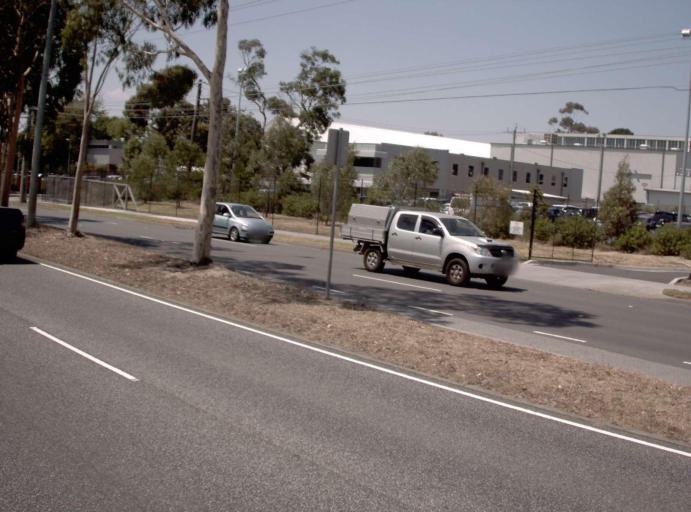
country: AU
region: Victoria
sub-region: Monash
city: Notting Hill
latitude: -37.8868
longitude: 145.1644
